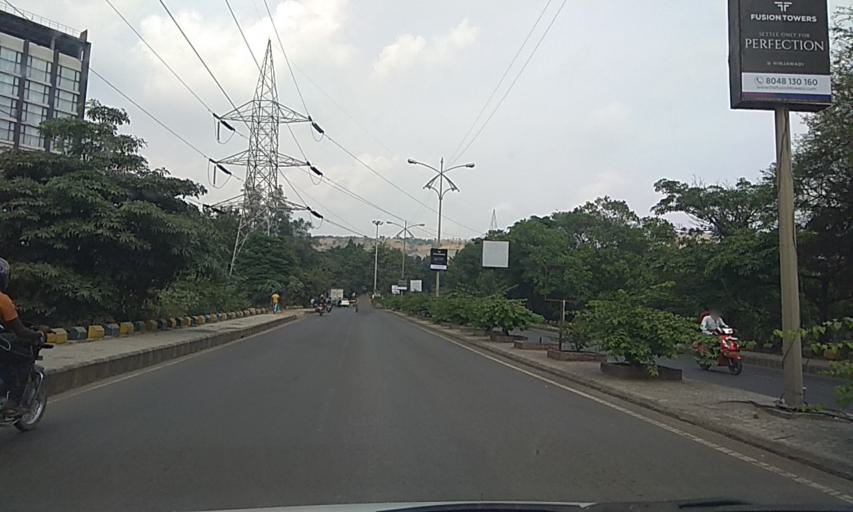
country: IN
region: Maharashtra
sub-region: Pune Division
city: Pimpri
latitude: 18.5924
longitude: 73.7074
